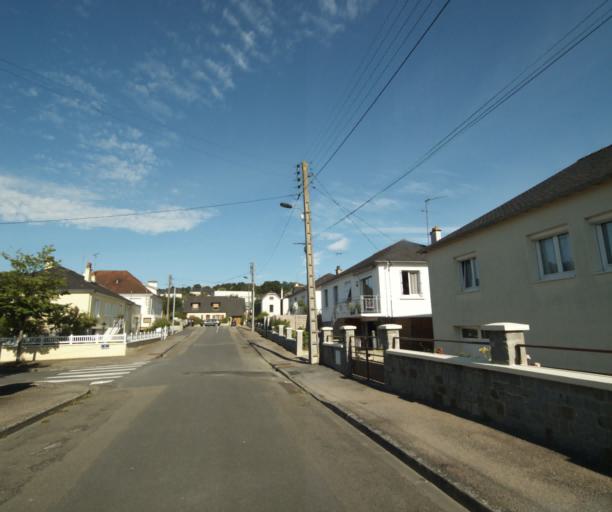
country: FR
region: Pays de la Loire
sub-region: Departement de la Mayenne
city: Laval
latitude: 48.0562
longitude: -0.7655
